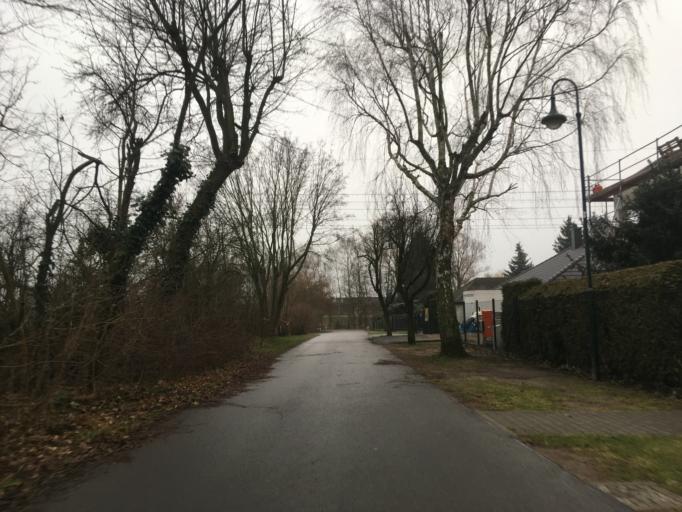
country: DE
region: Berlin
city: Buch
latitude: 52.6214
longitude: 13.5064
